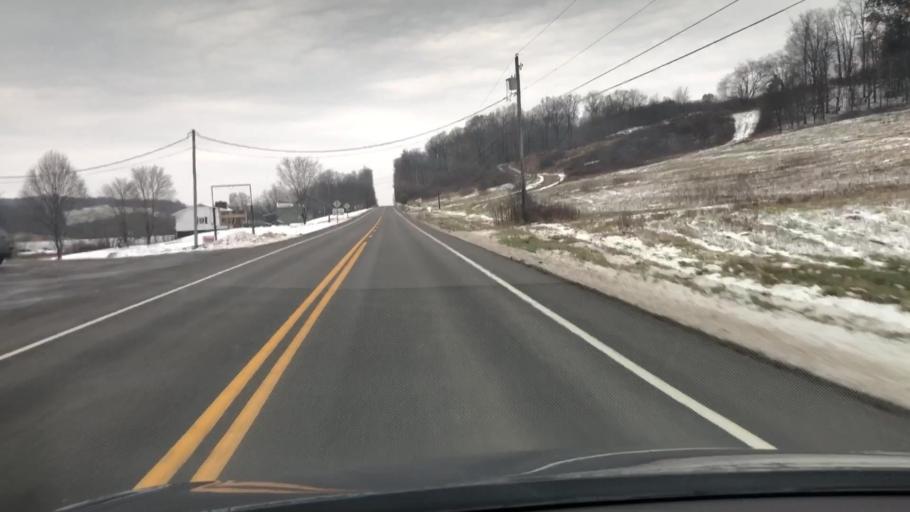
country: US
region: Pennsylvania
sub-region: Jefferson County
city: Brookville
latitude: 41.0696
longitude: -79.2392
